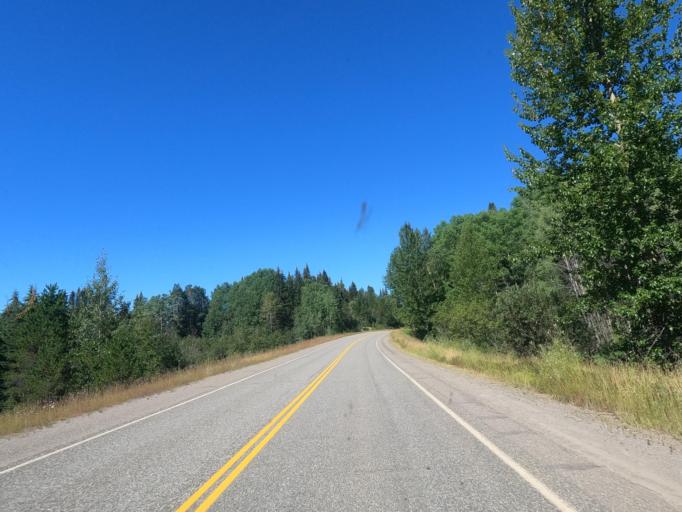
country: CA
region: British Columbia
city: Quesnel
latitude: 53.0535
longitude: -122.1607
